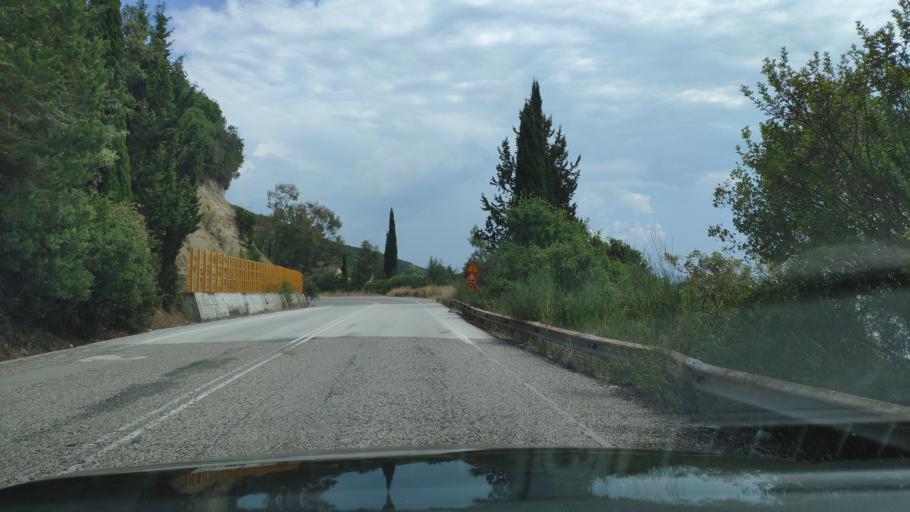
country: GR
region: West Greece
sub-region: Nomos Aitolias kai Akarnanias
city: Menidi
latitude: 39.0175
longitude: 21.1369
